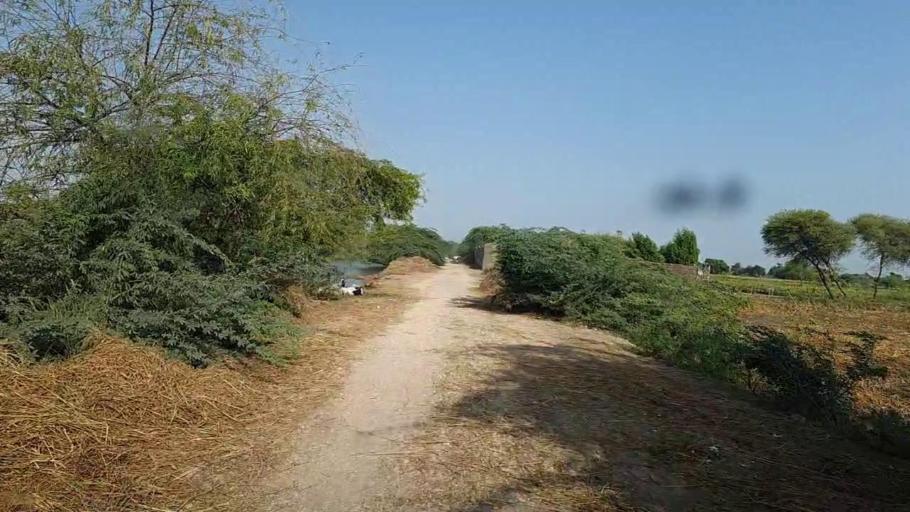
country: PK
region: Sindh
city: Bulri
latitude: 24.7742
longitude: 68.4275
